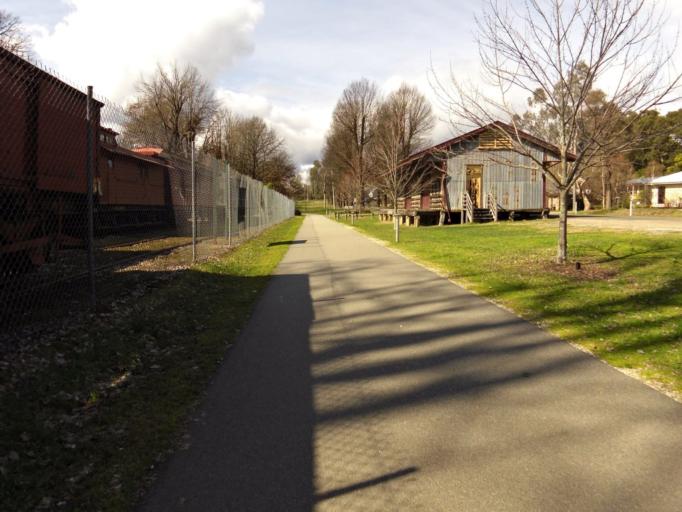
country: AU
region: Victoria
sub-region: Alpine
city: Mount Beauty
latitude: -36.7303
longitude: 146.9563
